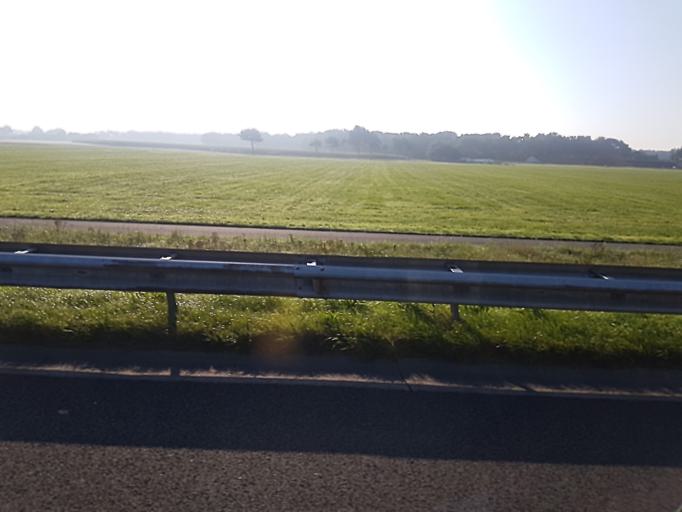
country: NL
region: North Brabant
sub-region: Gemeente Zundert
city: Zundert
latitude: 51.4728
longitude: 4.7292
